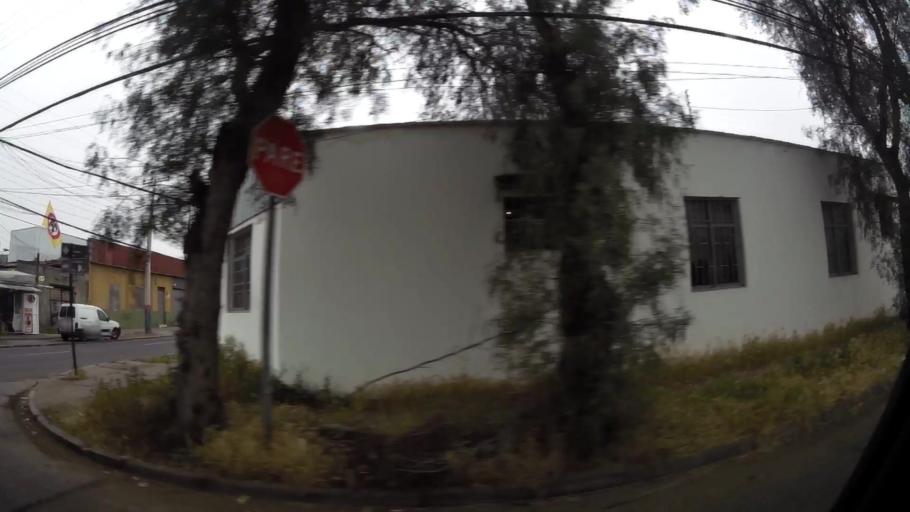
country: CL
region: Santiago Metropolitan
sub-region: Provincia de Santiago
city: Santiago
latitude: -33.4941
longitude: -70.6456
